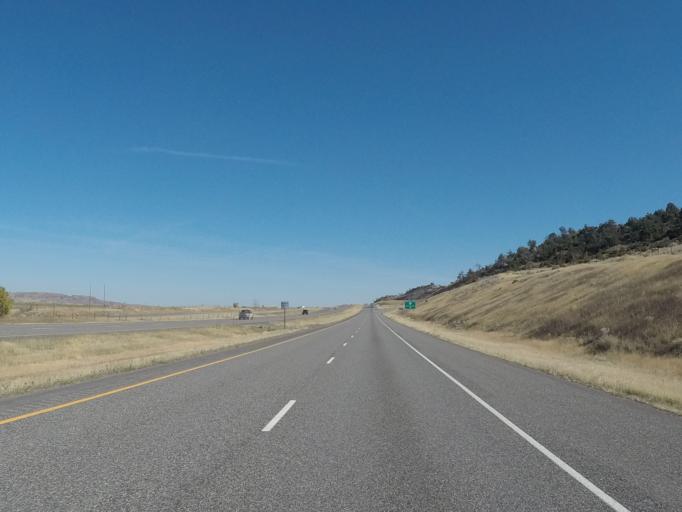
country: US
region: Montana
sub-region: Sweet Grass County
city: Big Timber
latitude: 45.7351
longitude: -110.2244
